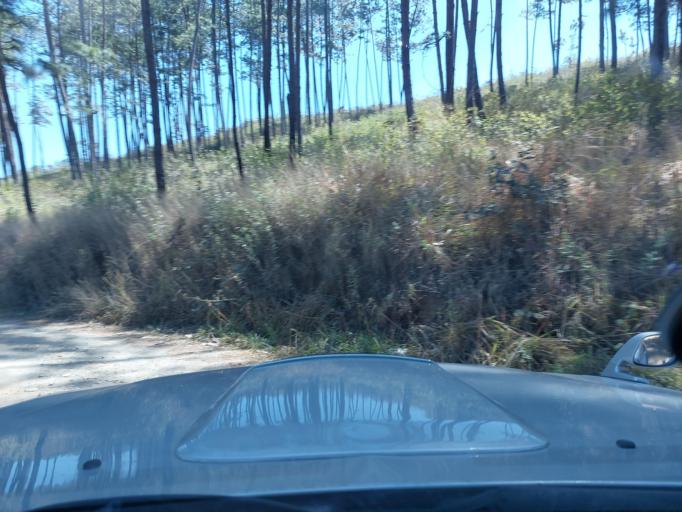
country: GT
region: Chimaltenango
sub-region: Municipio de Chimaltenango
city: Chimaltenango
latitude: 14.6518
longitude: -90.8315
